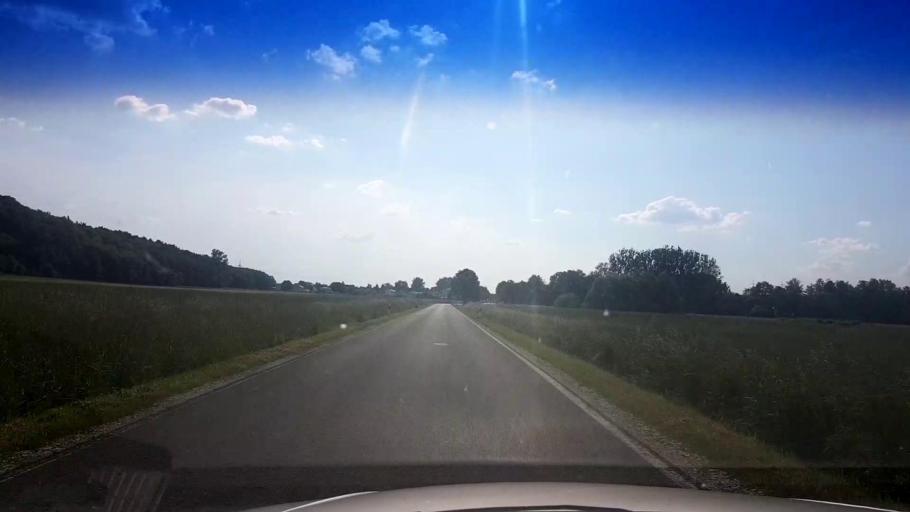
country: DE
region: Bavaria
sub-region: Upper Franconia
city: Memmelsdorf
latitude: 49.9419
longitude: 10.9823
